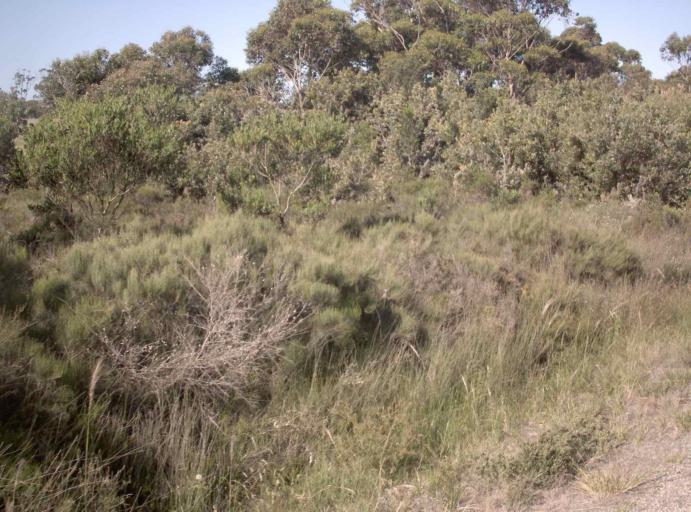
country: AU
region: Victoria
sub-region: East Gippsland
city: Lakes Entrance
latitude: -37.8009
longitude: 148.6436
